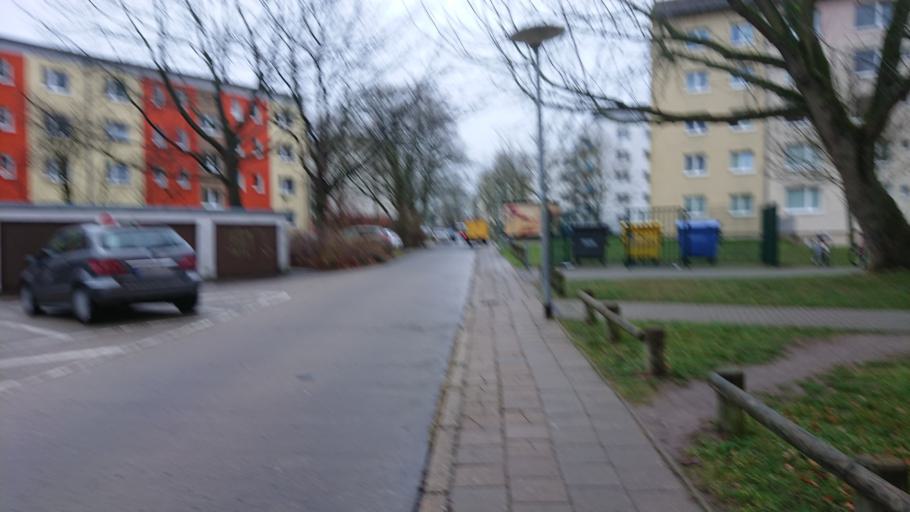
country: DE
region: Mecklenburg-Vorpommern
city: Rostock
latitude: 54.0749
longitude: 12.1122
